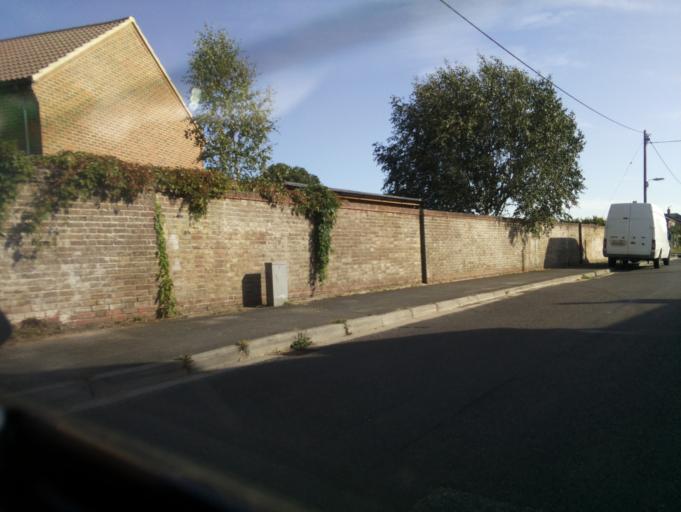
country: GB
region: England
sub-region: Hampshire
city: Chandlers Ford
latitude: 50.9799
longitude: -1.4356
